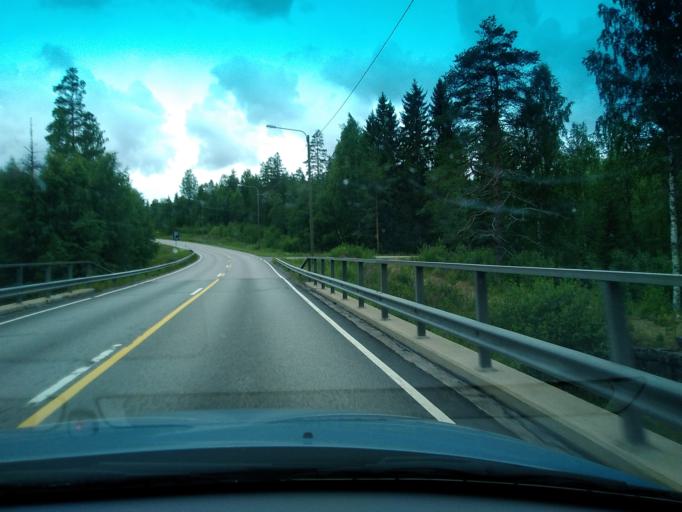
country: FI
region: Central Finland
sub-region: Saarijaervi-Viitasaari
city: Pylkoenmaeki
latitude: 62.6413
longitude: 24.8421
